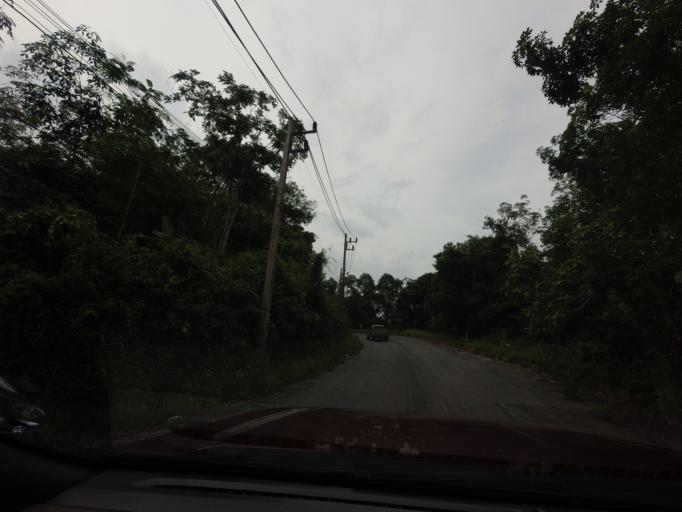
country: TH
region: Yala
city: Than To
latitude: 6.1383
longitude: 101.2942
